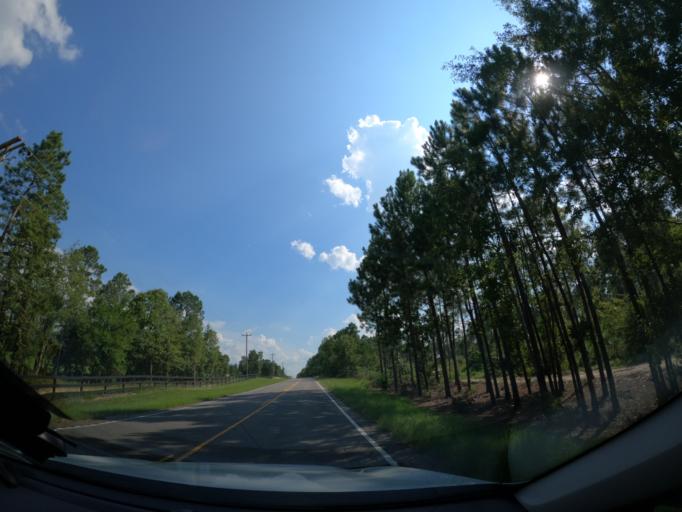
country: US
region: South Carolina
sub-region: Barnwell County
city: Williston
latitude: 33.5408
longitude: -81.4924
